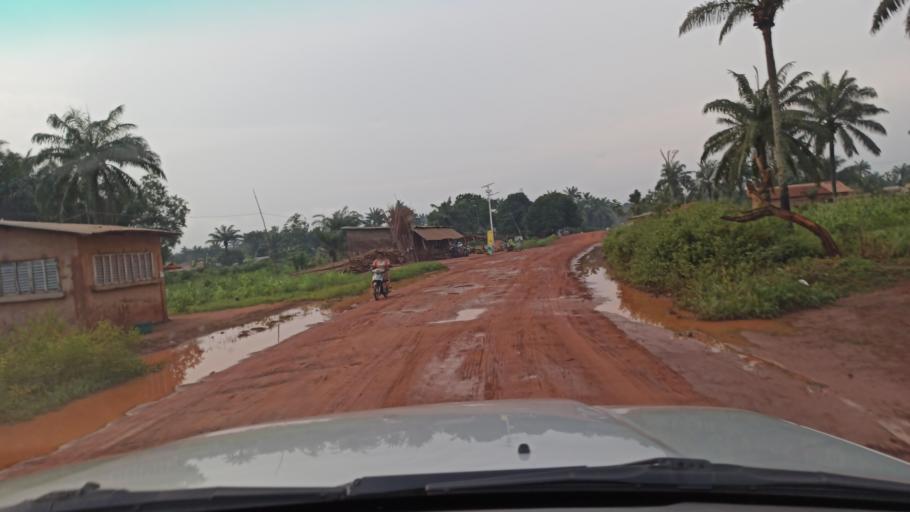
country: BJ
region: Queme
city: Porto-Novo
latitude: 6.5464
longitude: 2.6143
